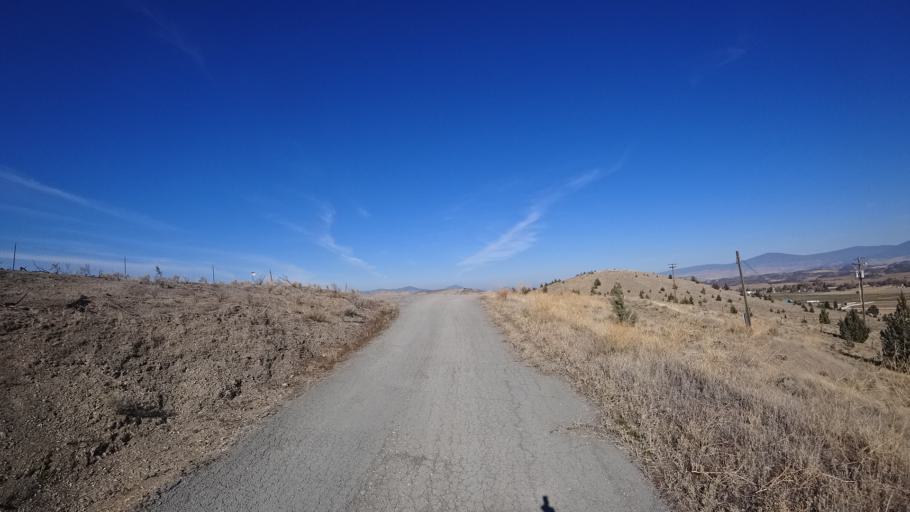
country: US
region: California
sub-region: Siskiyou County
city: Montague
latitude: 41.6360
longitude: -122.5404
